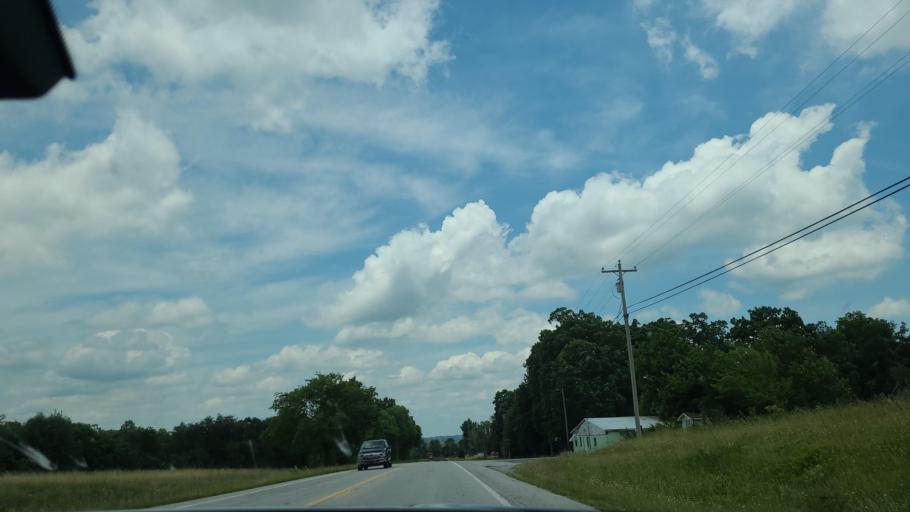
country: US
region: Tennessee
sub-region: Cumberland County
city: Lake Tansi
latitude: 35.7975
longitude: -85.0240
